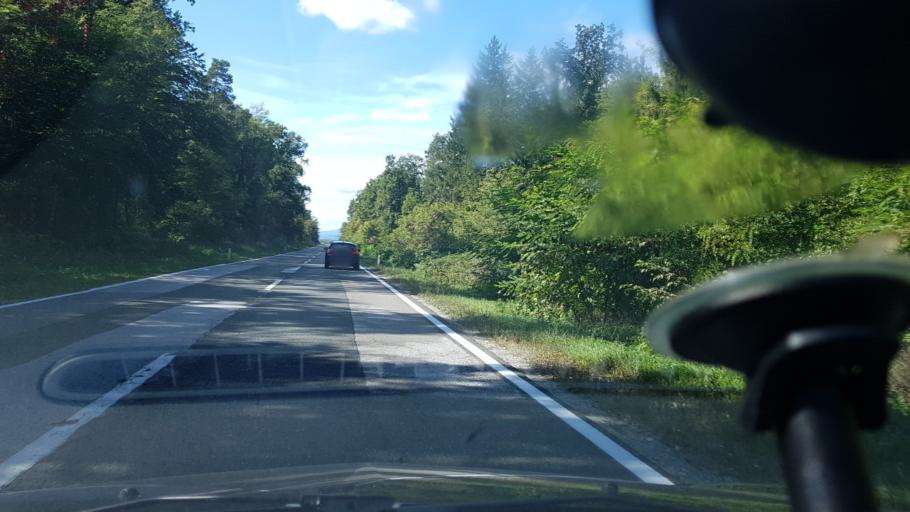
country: SI
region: Kidricevo
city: Kidricevo
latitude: 46.4101
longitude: 15.7622
